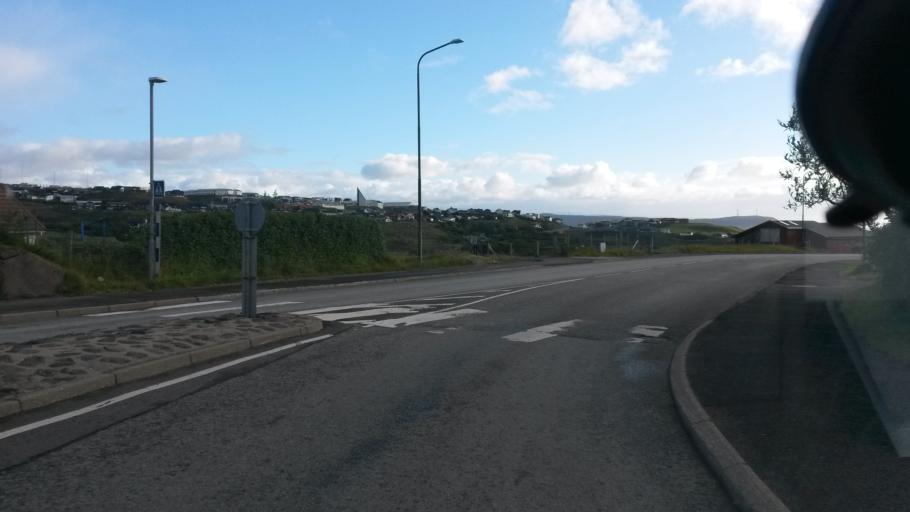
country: FO
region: Streymoy
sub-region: Torshavn
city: Torshavn
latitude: 62.0212
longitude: -6.7760
